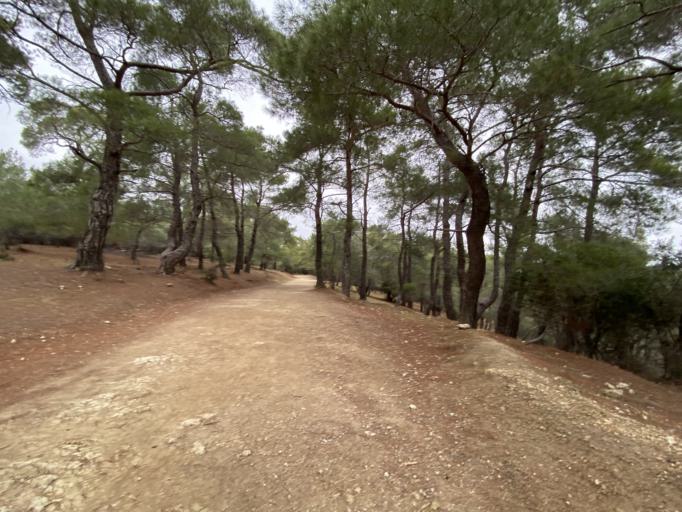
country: TR
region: Canakkale
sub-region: Merkez
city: Kucukkuyu
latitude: 39.5629
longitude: 26.6169
